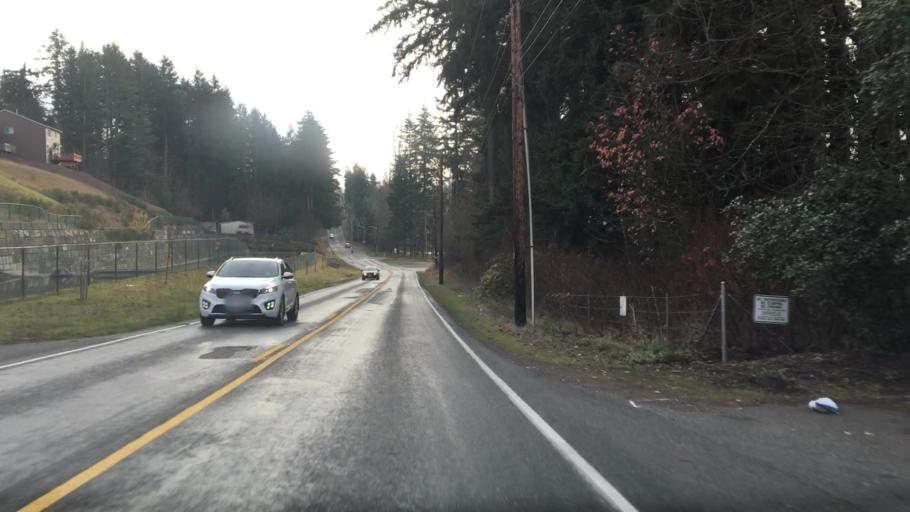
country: US
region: Washington
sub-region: Pierce County
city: Frederickson
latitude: 47.1167
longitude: -122.3253
